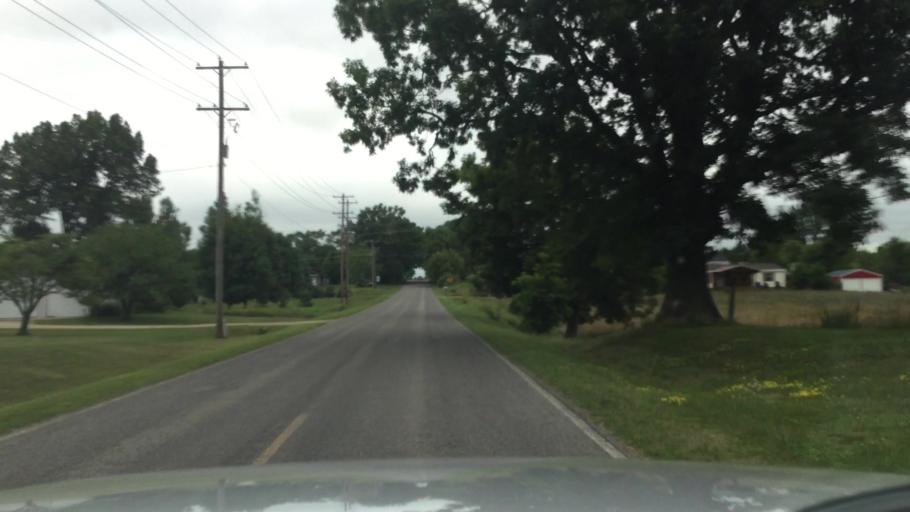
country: US
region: Michigan
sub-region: Montcalm County
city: Greenville
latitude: 43.1895
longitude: -85.2232
